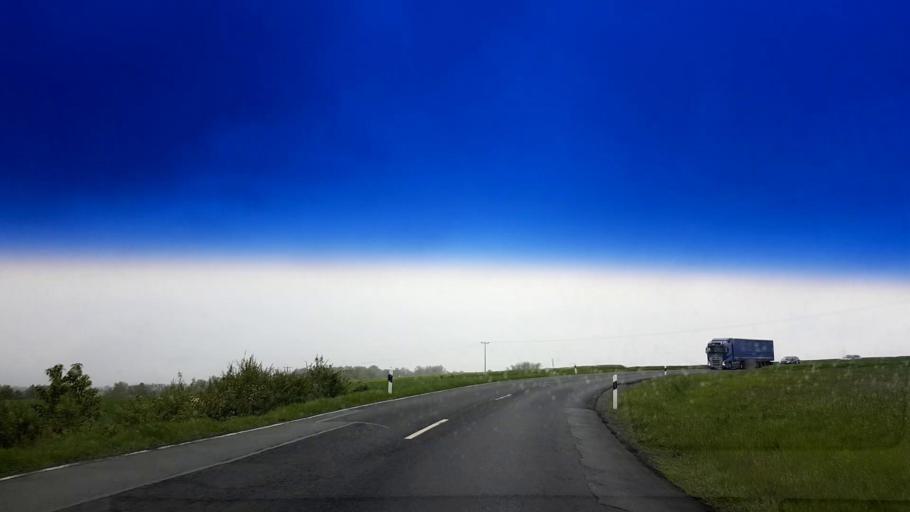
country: DE
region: Bavaria
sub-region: Upper Franconia
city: Bindlach
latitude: 50.0060
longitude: 11.6303
